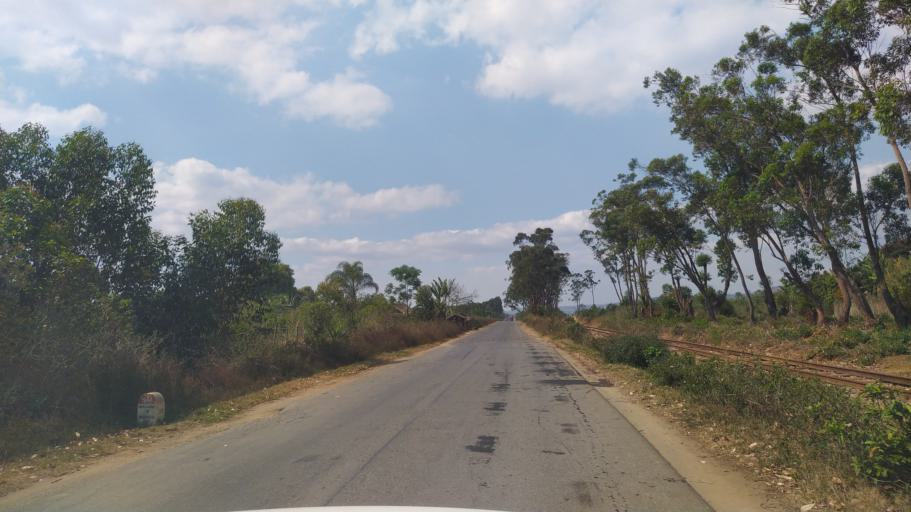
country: MG
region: Alaotra Mangoro
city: Moramanga
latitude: -18.7786
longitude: 48.2488
